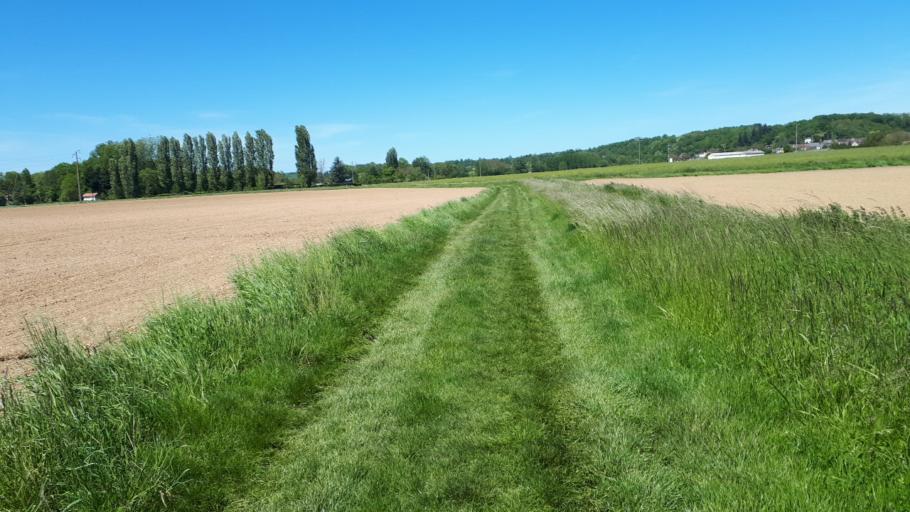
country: FR
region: Centre
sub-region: Departement du Loir-et-Cher
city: Villiers-sur-Loir
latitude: 47.8023
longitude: 0.9865
